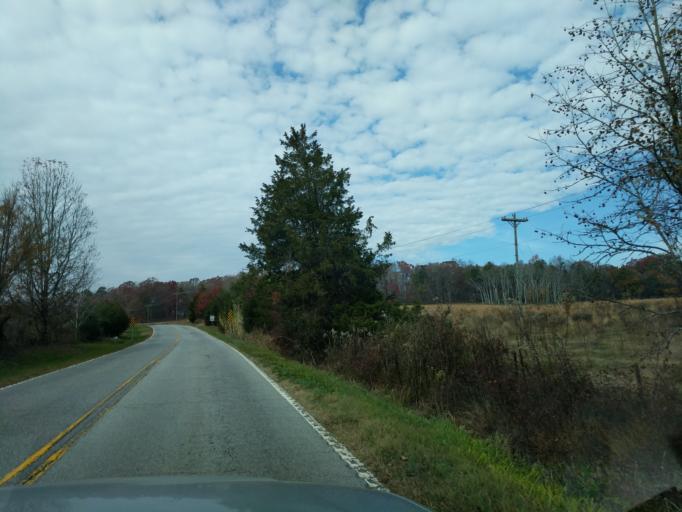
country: US
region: South Carolina
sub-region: Anderson County
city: Piedmont
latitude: 34.7272
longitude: -82.5303
